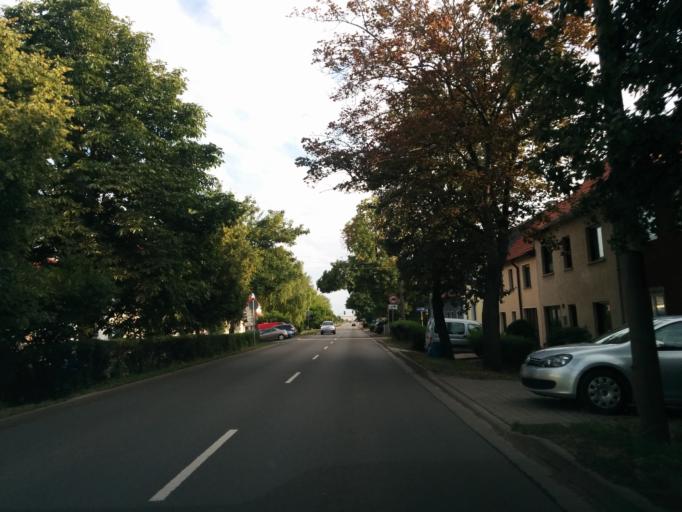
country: DE
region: Thuringia
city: Gebesee
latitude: 51.1136
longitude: 10.9309
